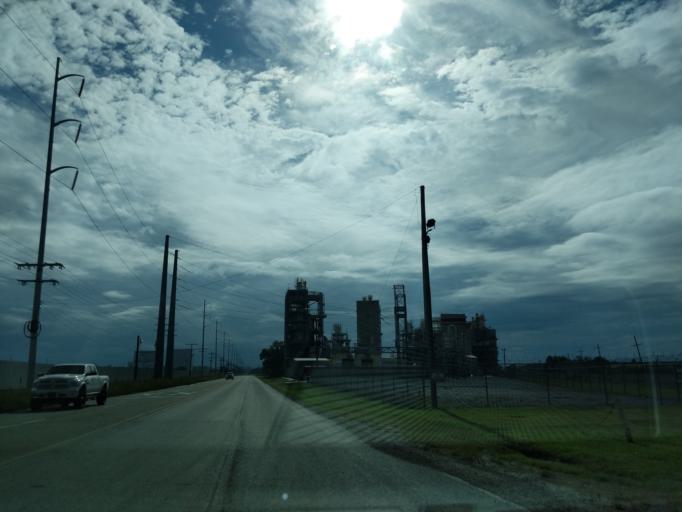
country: US
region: Louisiana
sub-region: Saint Bernard Parish
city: Chalmette
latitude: 30.0365
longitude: -89.9066
